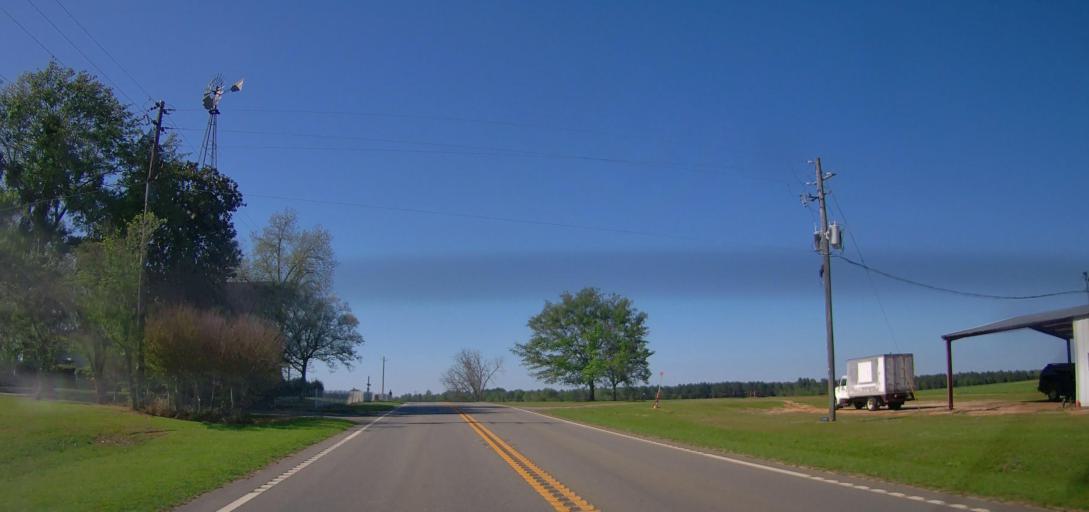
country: US
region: Georgia
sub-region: Pulaski County
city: Hawkinsville
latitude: 32.1449
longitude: -83.5112
